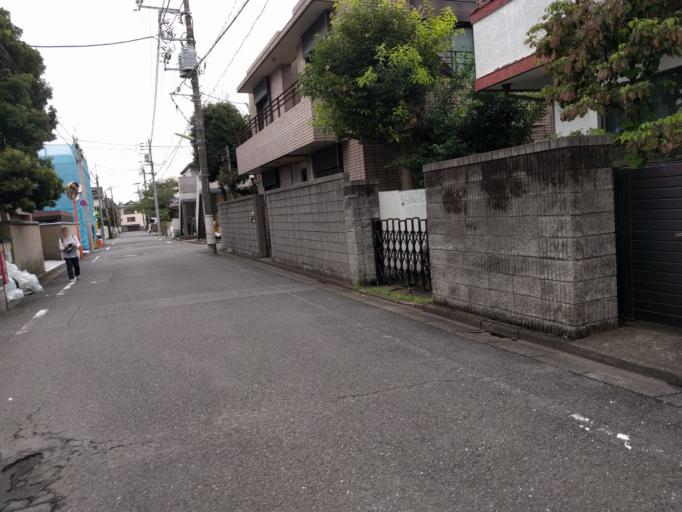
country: JP
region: Tokyo
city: Tokyo
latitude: 35.6297
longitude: 139.6539
